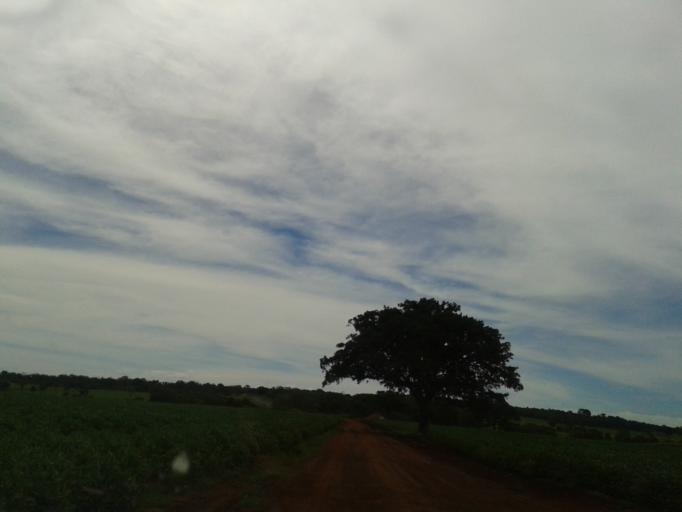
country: BR
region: Minas Gerais
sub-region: Capinopolis
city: Capinopolis
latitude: -18.7744
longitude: -49.8073
